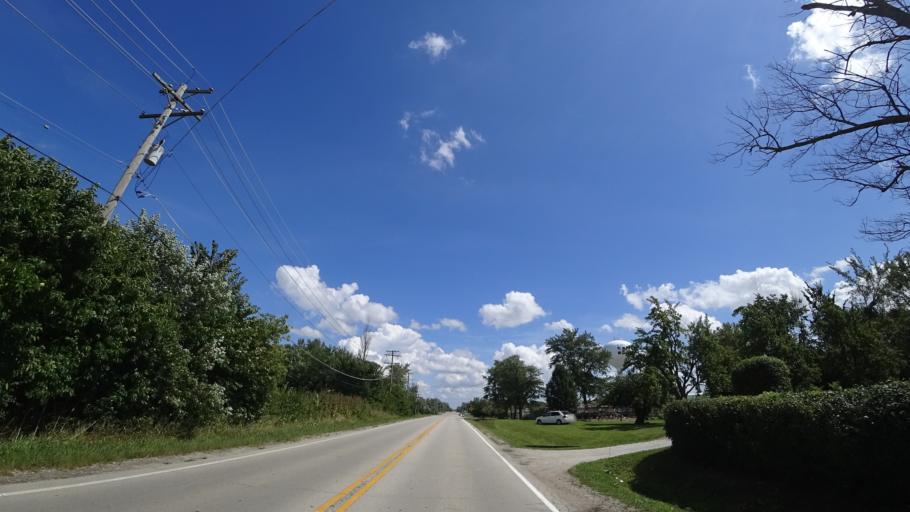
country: US
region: Illinois
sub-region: Cook County
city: Country Club Hills
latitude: 41.5571
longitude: -87.7392
